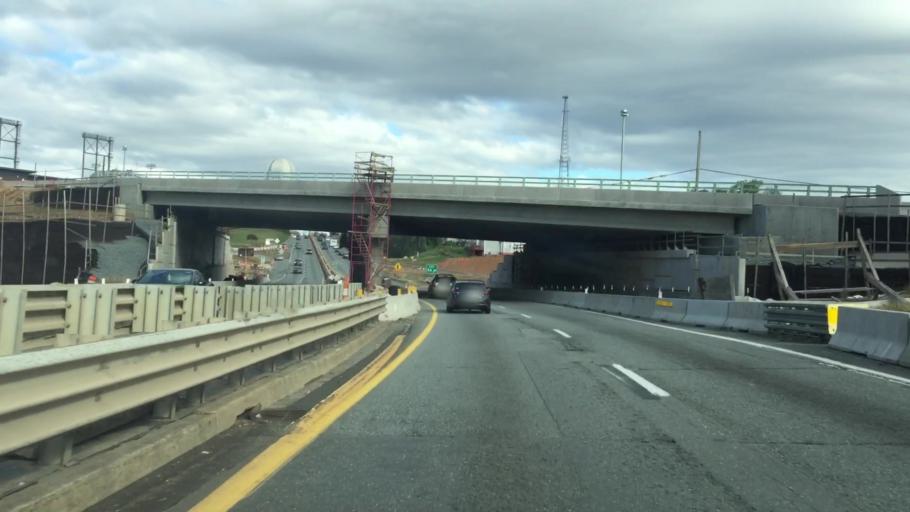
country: US
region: North Carolina
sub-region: Forsyth County
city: Winston-Salem
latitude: 36.0893
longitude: -80.2583
